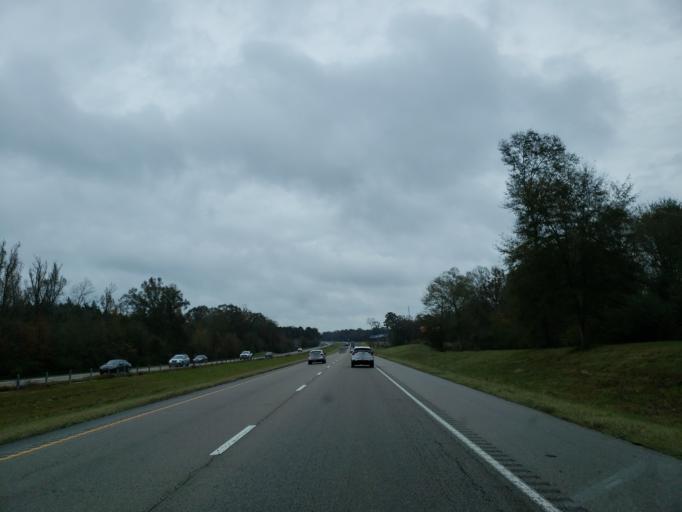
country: US
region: Mississippi
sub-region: Jones County
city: Ellisville
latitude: 31.5953
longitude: -89.2276
